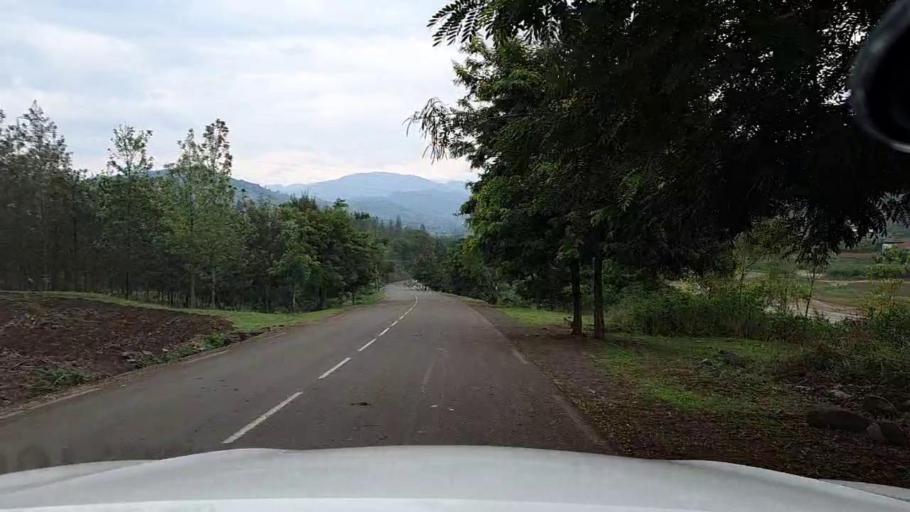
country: BI
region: Cibitoke
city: Cibitoke
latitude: -2.7337
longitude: 29.0386
